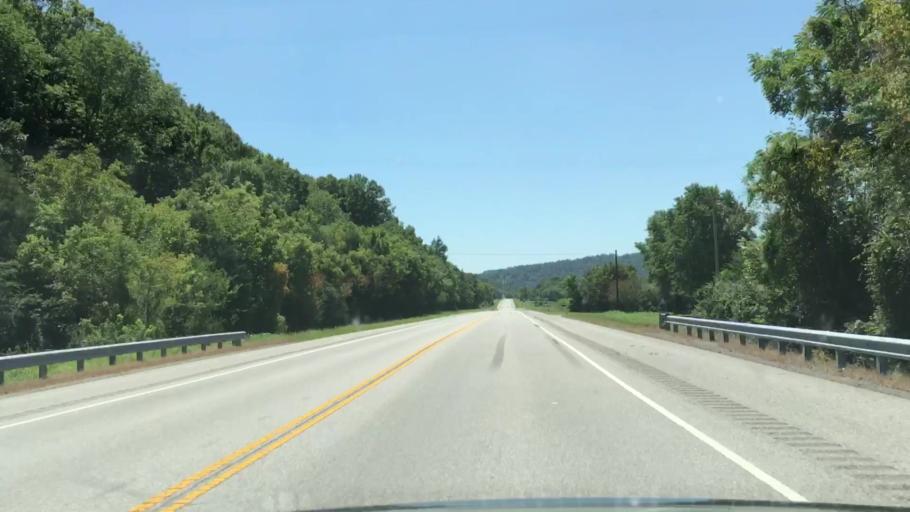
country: US
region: Tennessee
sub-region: Jackson County
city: Gainesboro
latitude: 36.3965
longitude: -85.6346
